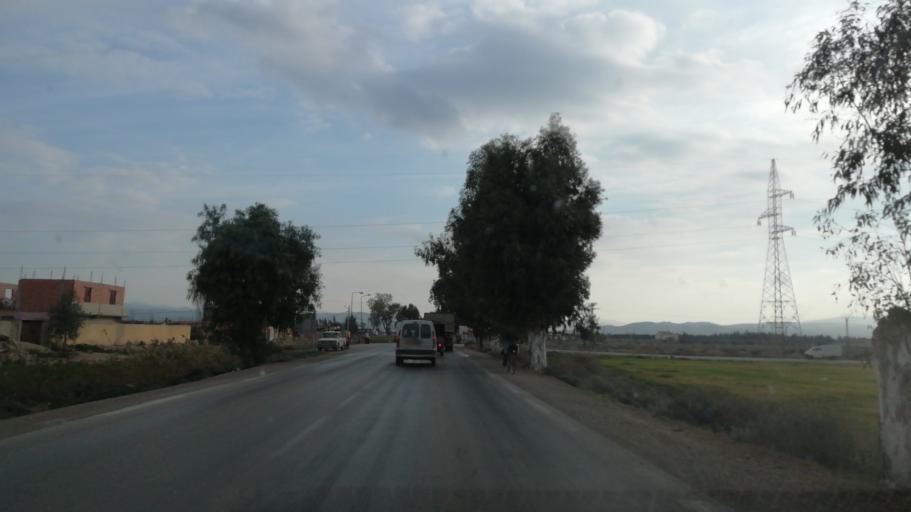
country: DZ
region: Mascara
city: Mascara
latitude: 35.6324
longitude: 0.0611
